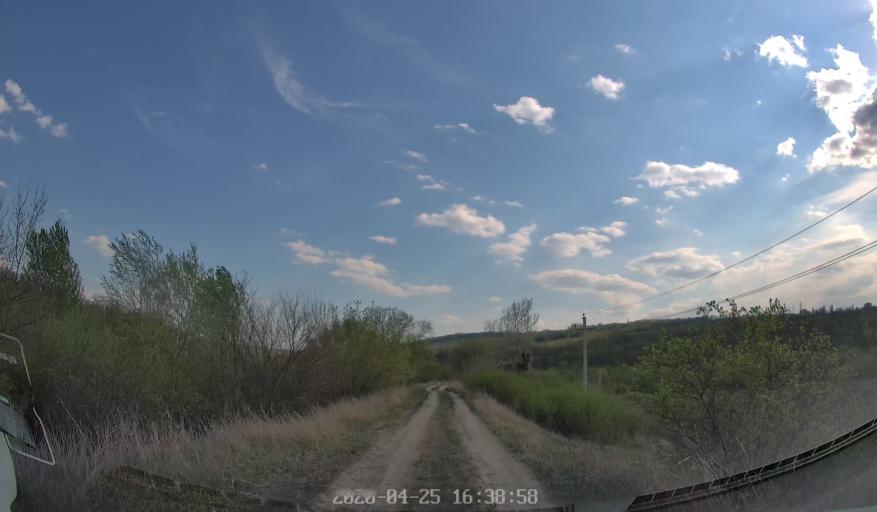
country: MD
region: Chisinau
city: Vadul lui Voda
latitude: 47.1097
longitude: 29.0642
